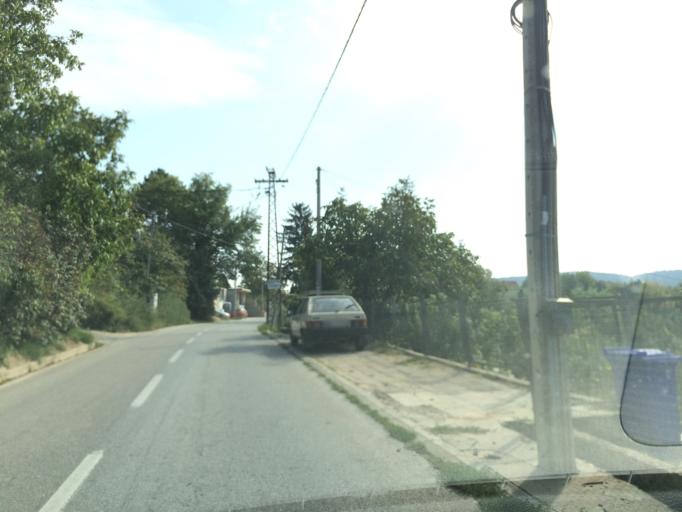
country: RS
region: Autonomna Pokrajina Vojvodina
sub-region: Juznobacki Okrug
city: Novi Sad
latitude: 45.2042
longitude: 19.8323
